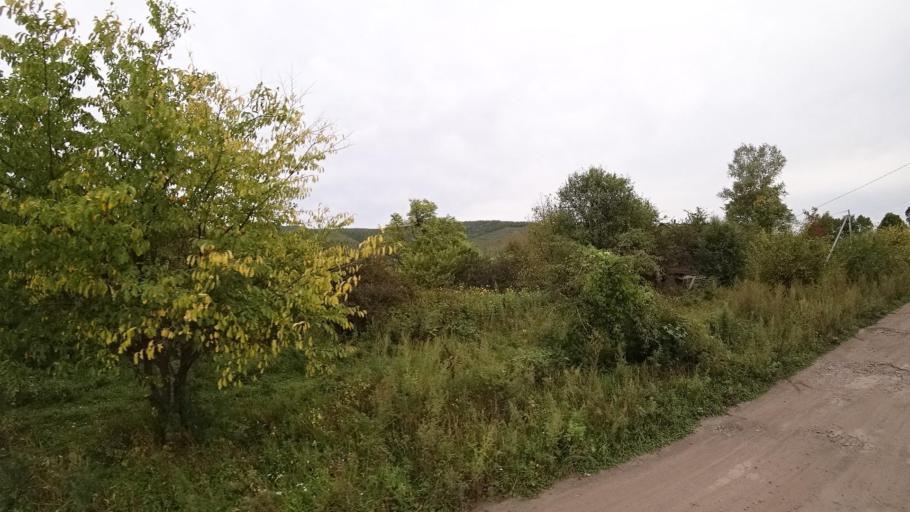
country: RU
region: Jewish Autonomous Oblast
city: Khingansk
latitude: 49.0399
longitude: 131.0496
